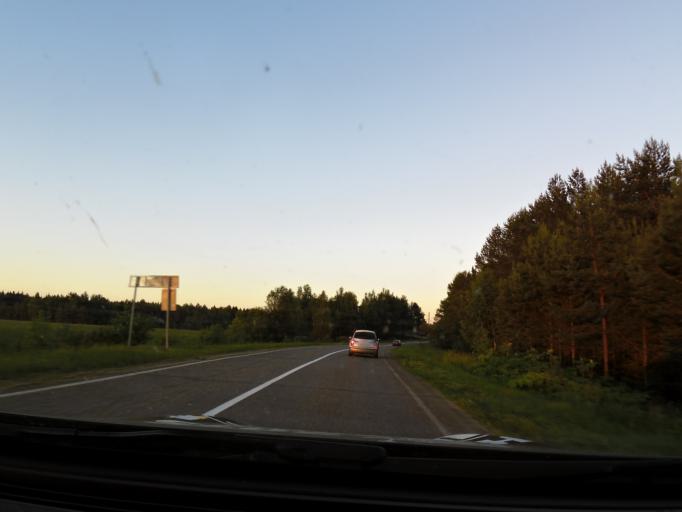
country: RU
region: Jaroslavl
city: Lyubim
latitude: 58.3493
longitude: 40.8151
